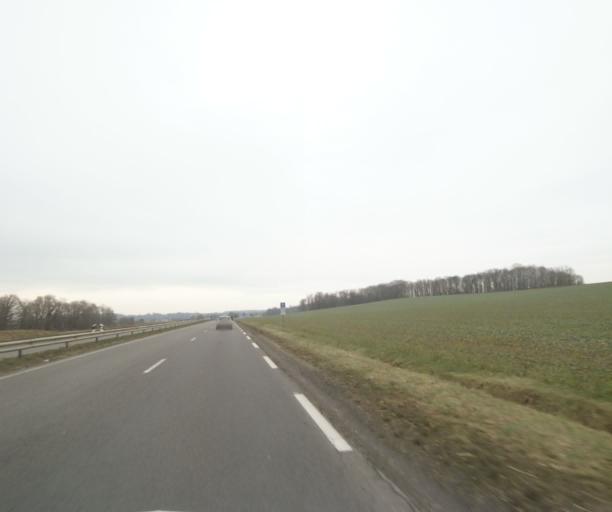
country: FR
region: Lorraine
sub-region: Departement de la Meuse
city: Ancerville
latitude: 48.6092
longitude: 5.0122
